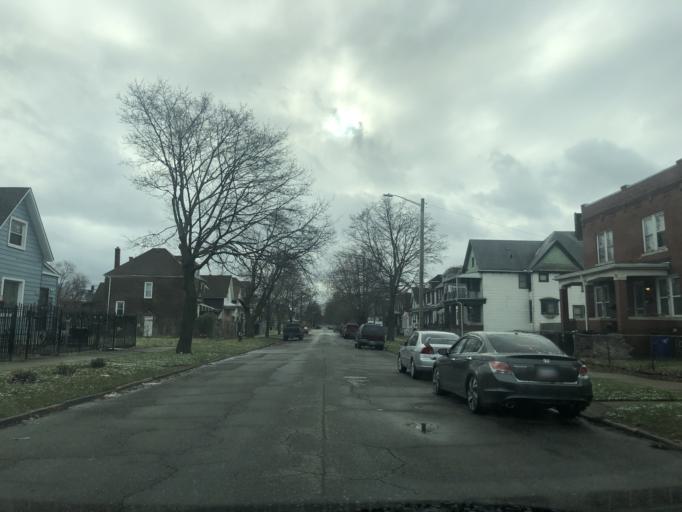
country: US
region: Michigan
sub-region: Wayne County
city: River Rouge
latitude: 42.3142
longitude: -83.1057
